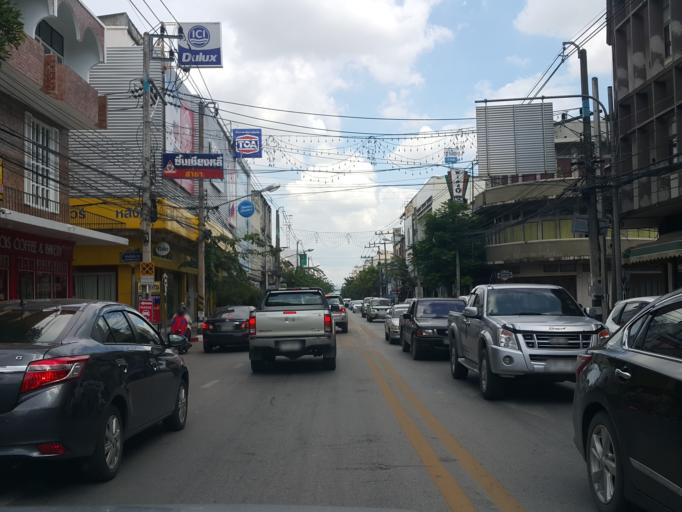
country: TH
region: Chiang Mai
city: Chiang Mai
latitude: 18.7876
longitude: 99.0058
